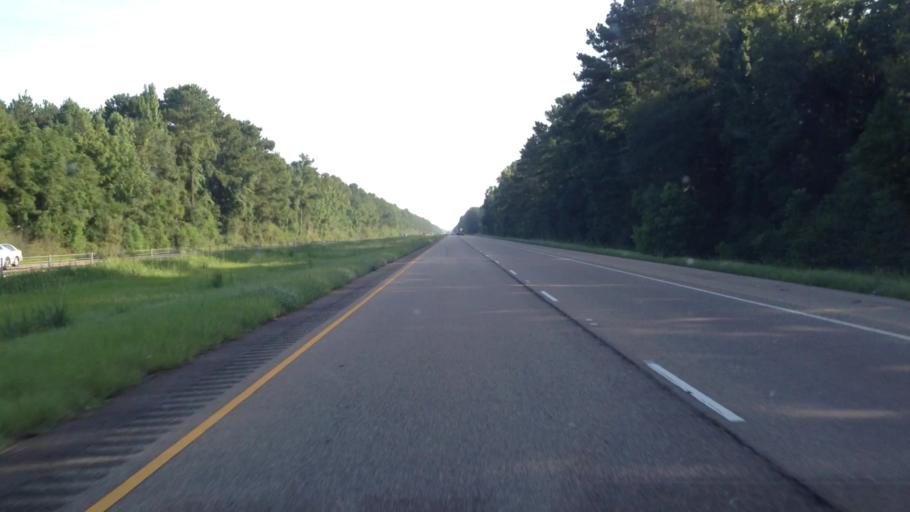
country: US
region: Louisiana
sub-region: Tangipahoa Parish
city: Amite
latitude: 30.6856
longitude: -90.5326
